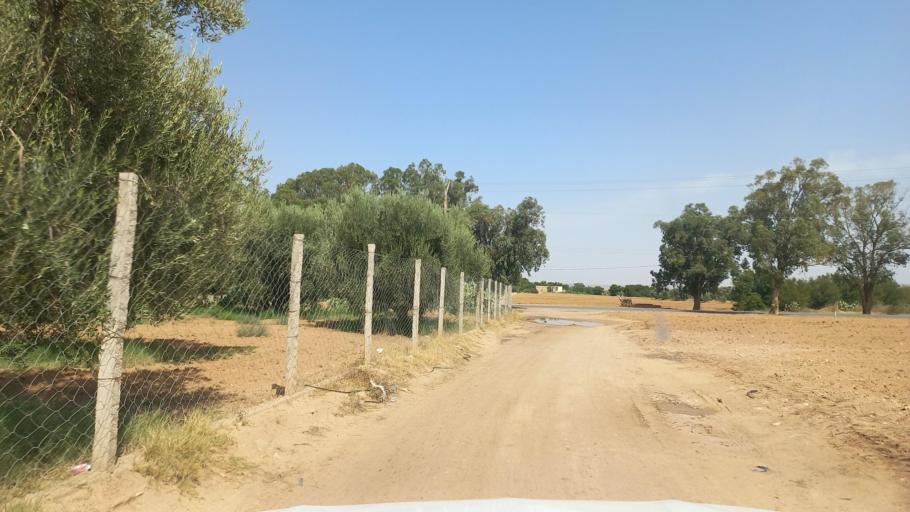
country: TN
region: Al Qasrayn
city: Kasserine
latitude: 35.2602
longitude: 9.0424
